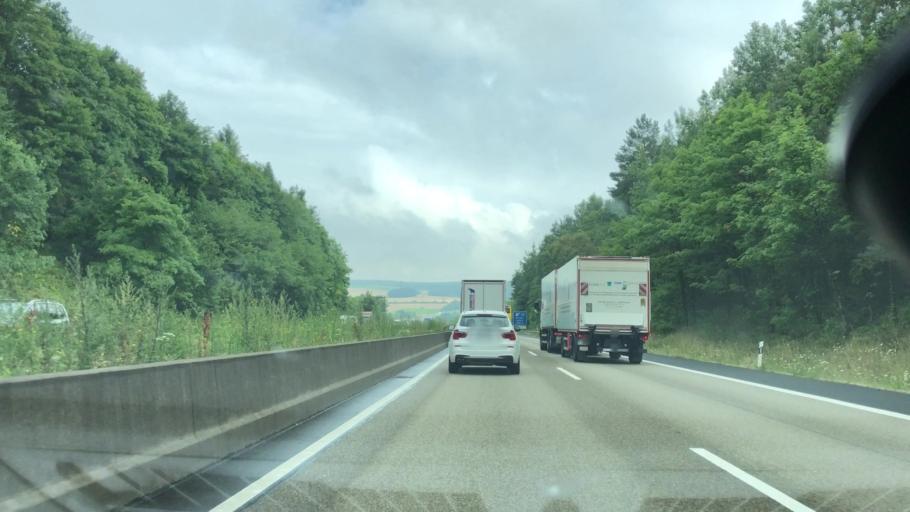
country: DE
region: Hesse
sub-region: Regierungsbezirk Kassel
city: Burghaun
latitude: 50.6484
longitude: 9.6826
